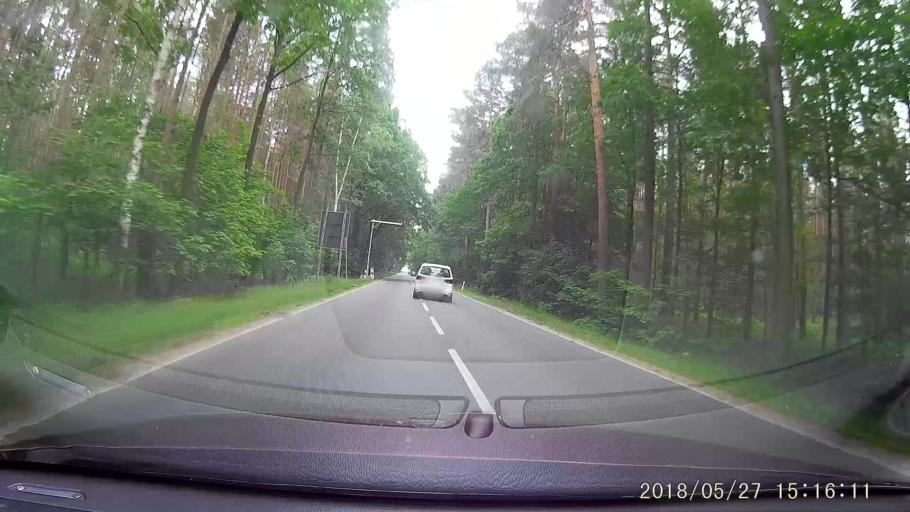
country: DE
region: Saxony
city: Niesky
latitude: 51.2785
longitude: 14.8206
